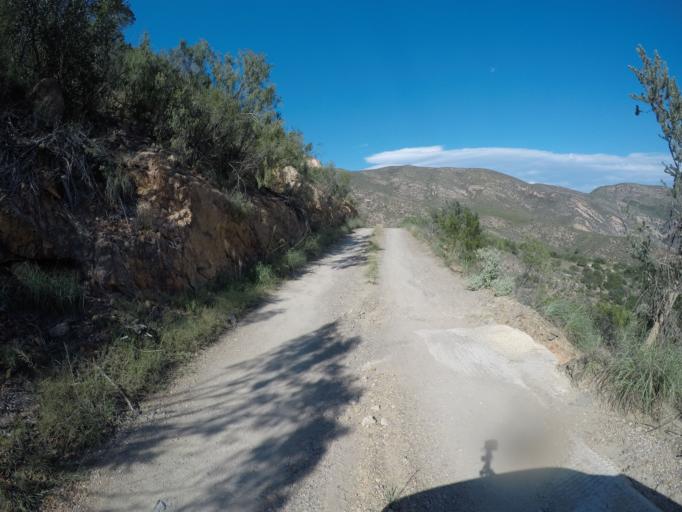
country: ZA
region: Eastern Cape
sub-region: Cacadu District Municipality
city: Kareedouw
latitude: -33.6437
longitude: 24.4619
